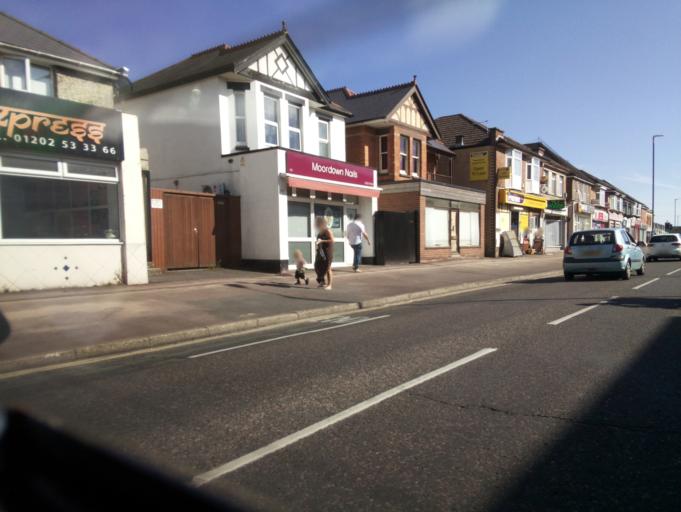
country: GB
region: England
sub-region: Bournemouth
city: Bournemouth
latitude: 50.7539
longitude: -1.8756
